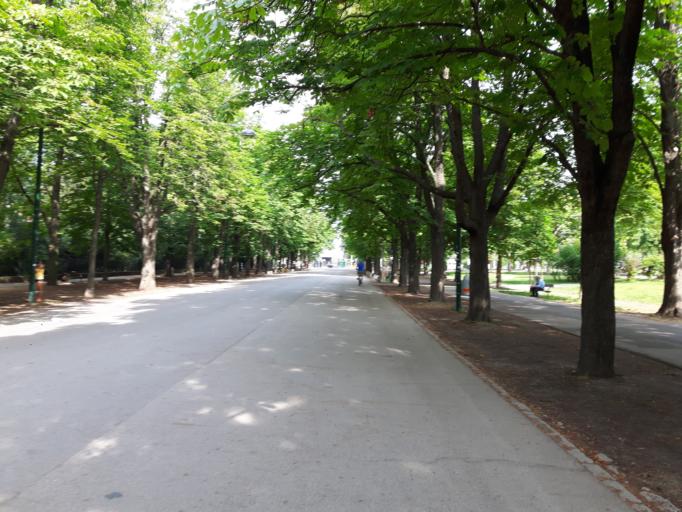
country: AT
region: Vienna
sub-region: Wien Stadt
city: Vienna
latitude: 48.2158
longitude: 16.3949
